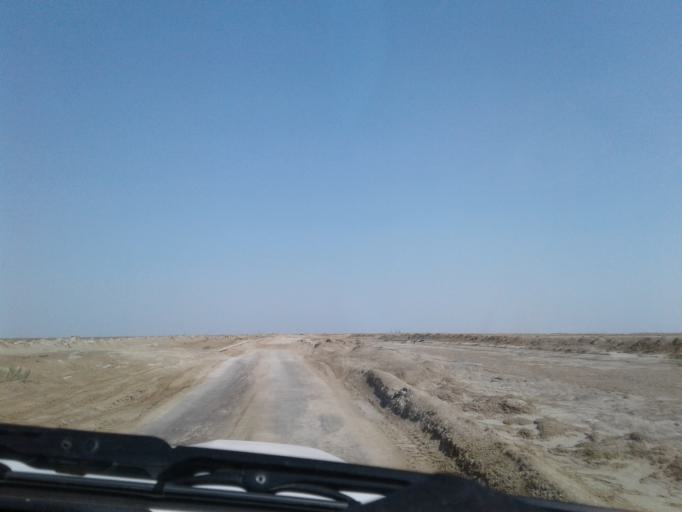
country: IR
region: Golestan
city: Gomishan
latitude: 37.8304
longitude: 53.9215
